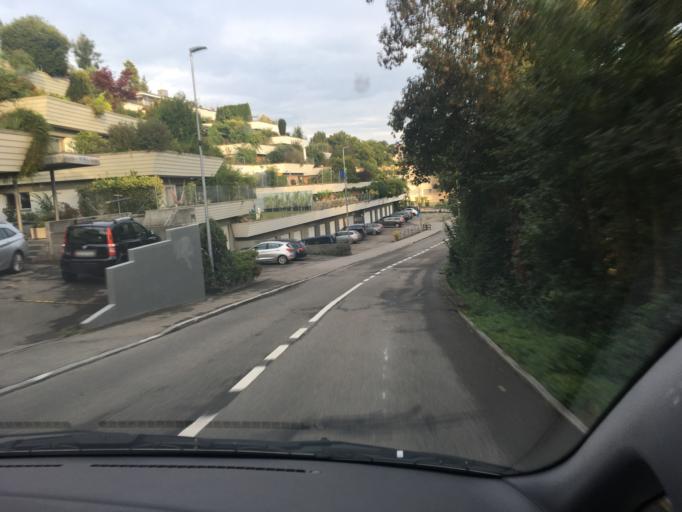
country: CH
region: Bern
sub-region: Bern-Mittelland District
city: Kirchlindach
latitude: 46.9738
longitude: 7.4319
